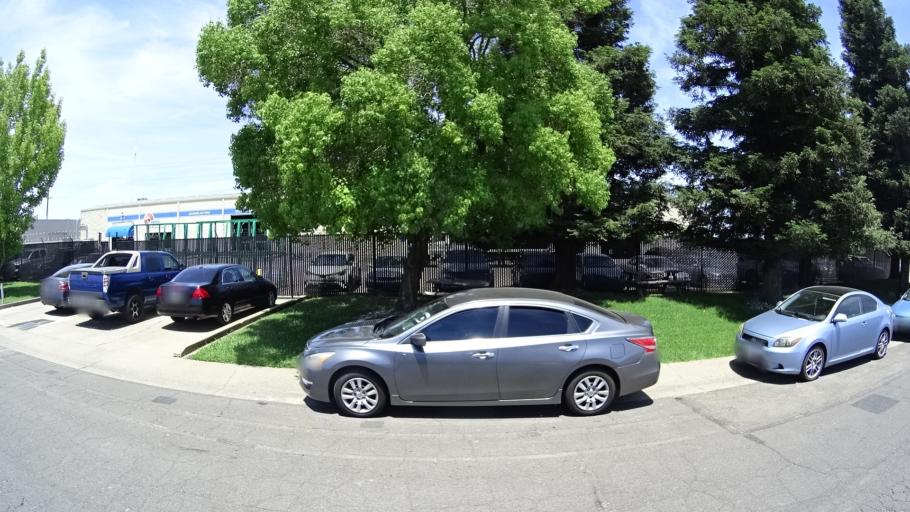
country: US
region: California
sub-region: Sacramento County
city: Rosemont
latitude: 38.5317
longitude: -121.3839
